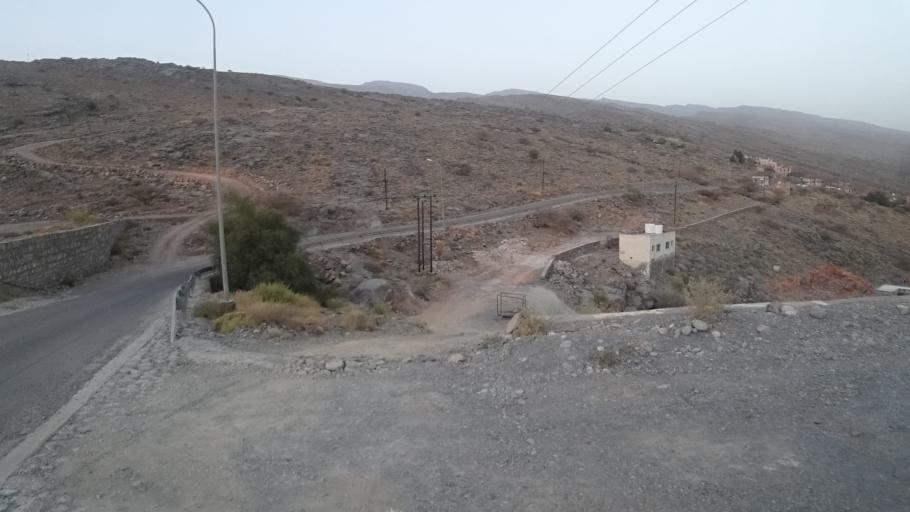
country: OM
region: Muhafazat ad Dakhiliyah
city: Bahla'
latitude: 23.1399
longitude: 57.3072
